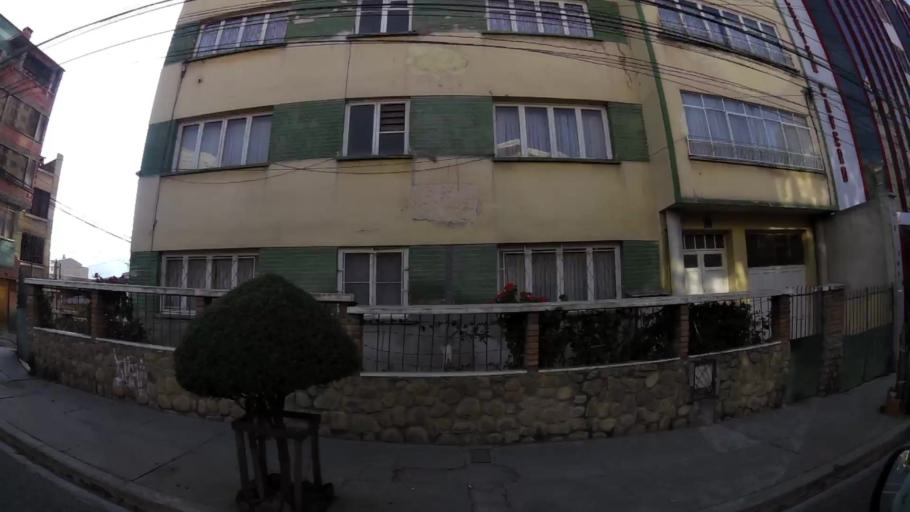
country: BO
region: La Paz
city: La Paz
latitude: -16.4893
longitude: -68.1224
